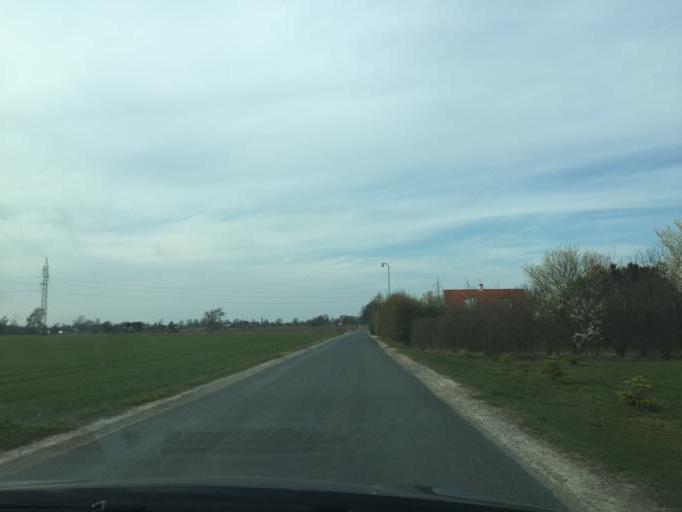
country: DK
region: South Denmark
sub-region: Faaborg-Midtfyn Kommune
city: Arslev
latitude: 55.3265
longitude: 10.5164
